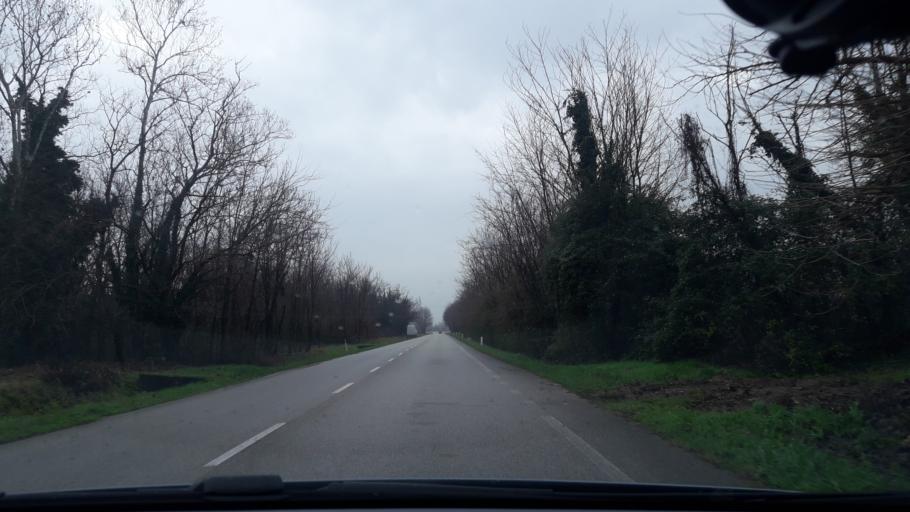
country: IT
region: Friuli Venezia Giulia
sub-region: Provincia di Udine
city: Colloredo di Prato
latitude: 46.0631
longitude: 13.1333
